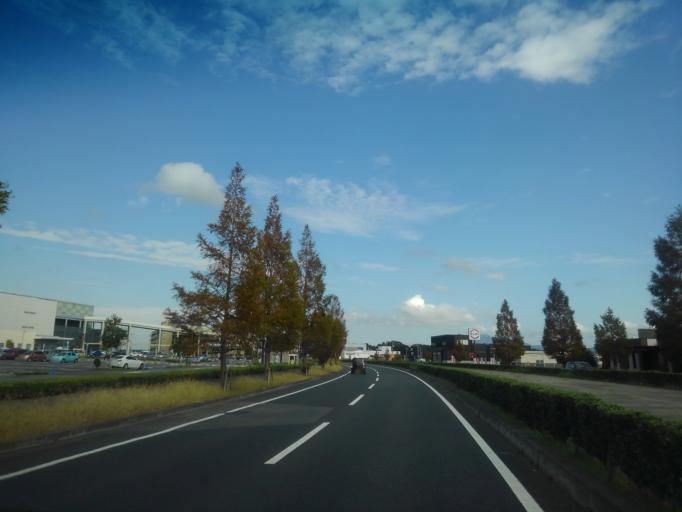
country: JP
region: Ibaraki
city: Naka
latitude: 36.0858
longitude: 140.0865
